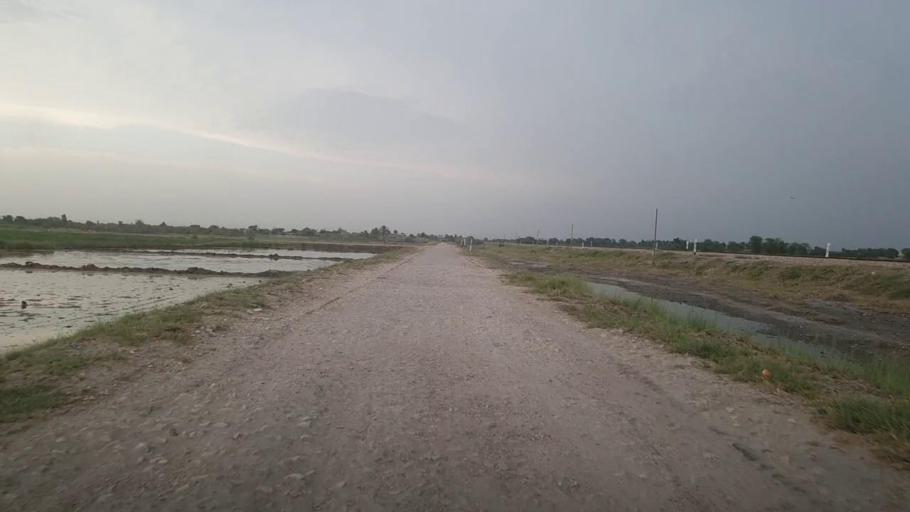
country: PK
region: Sindh
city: Karaundi
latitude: 26.9973
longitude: 68.3496
